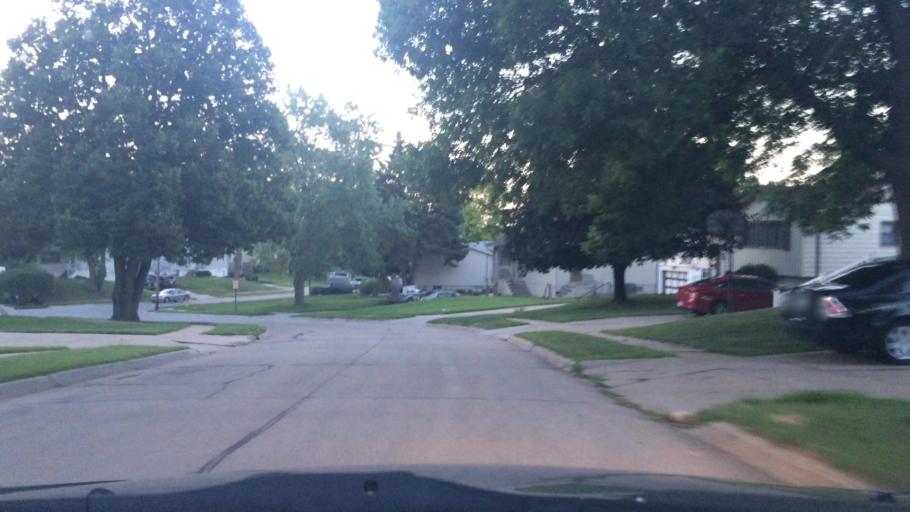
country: US
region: Nebraska
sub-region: Sarpy County
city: La Vista
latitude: 41.1867
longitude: -96.0492
